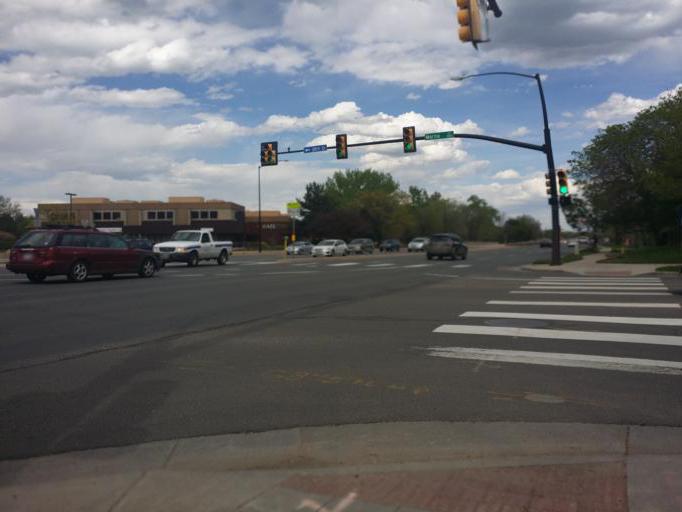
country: US
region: Colorado
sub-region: Boulder County
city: Boulder
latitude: 40.0143
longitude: -105.2467
